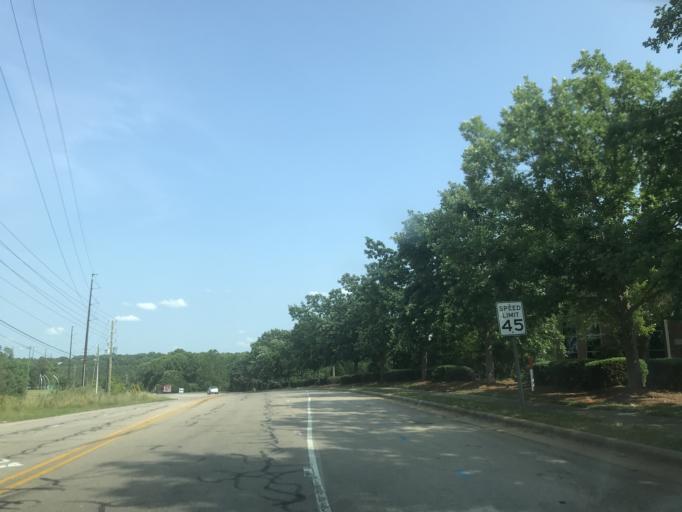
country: US
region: North Carolina
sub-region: Wake County
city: Cary
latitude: 35.8013
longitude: -78.7314
